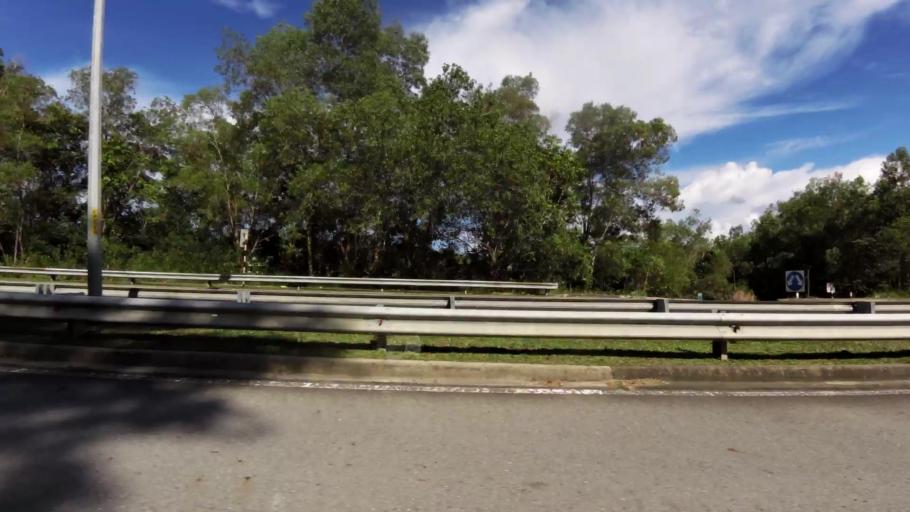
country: BN
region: Brunei and Muara
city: Bandar Seri Begawan
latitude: 4.9765
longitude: 114.9320
